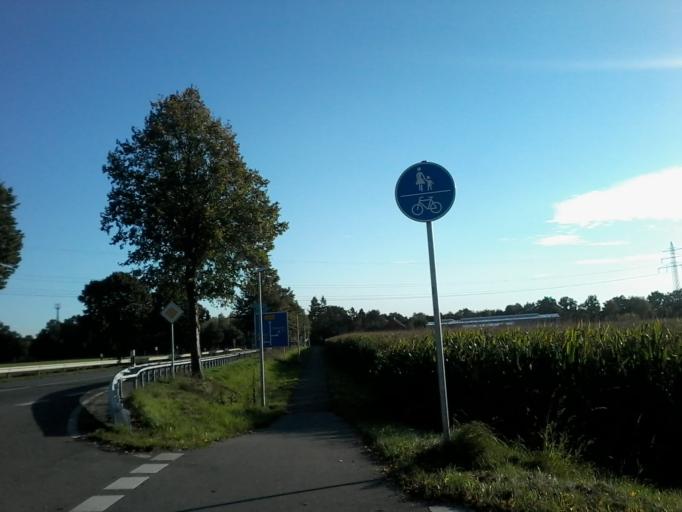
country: DE
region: Lower Saxony
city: Achim
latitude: 53.0271
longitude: 9.0314
